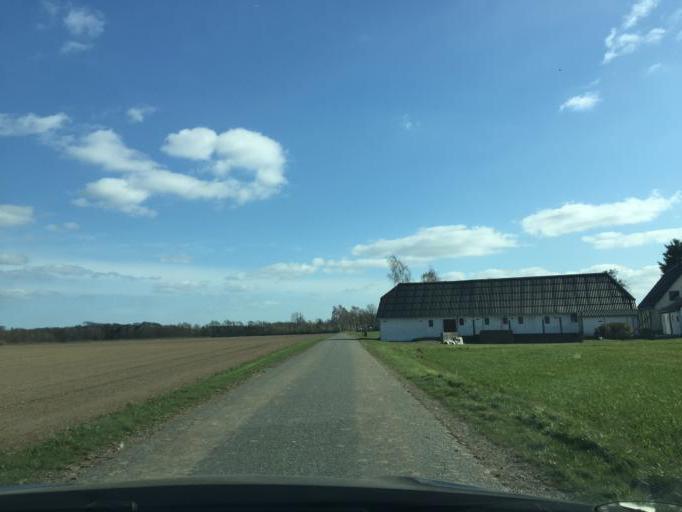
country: DK
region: South Denmark
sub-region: Kerteminde Kommune
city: Langeskov
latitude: 55.3003
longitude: 10.5663
